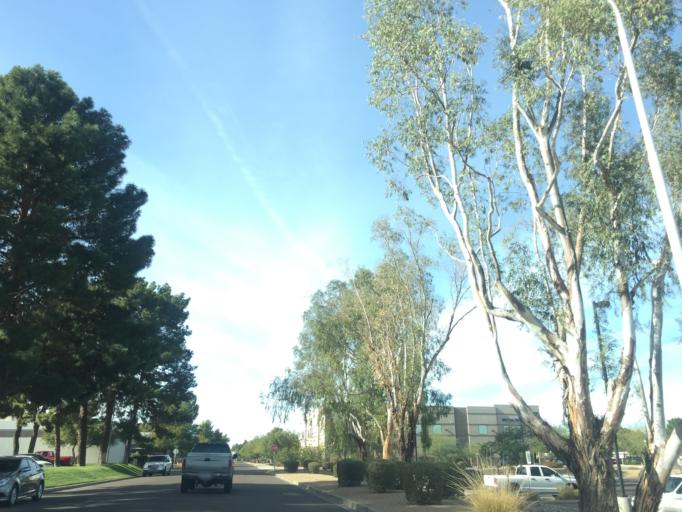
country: US
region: Arizona
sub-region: Maricopa County
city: Guadalupe
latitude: 33.3965
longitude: -111.9697
